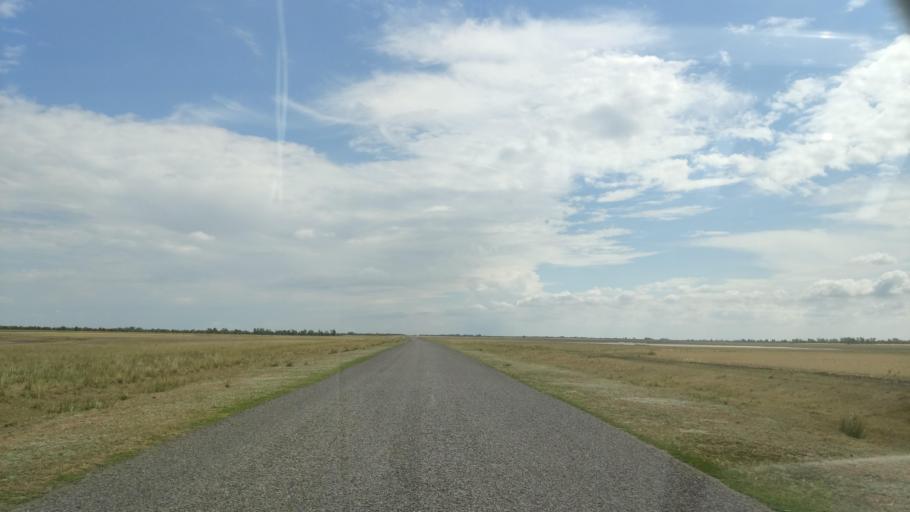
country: KZ
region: Pavlodar
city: Pavlodar
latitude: 52.6353
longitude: 76.9182
